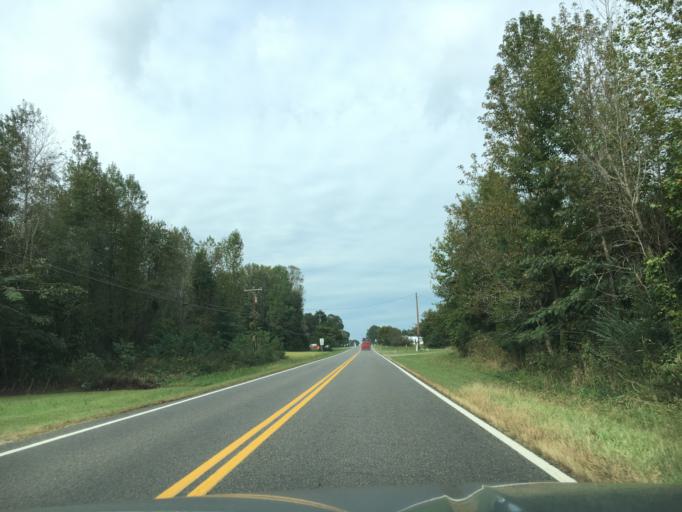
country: US
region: Virginia
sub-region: Goochland County
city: Goochland
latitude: 37.7203
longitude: -77.8265
